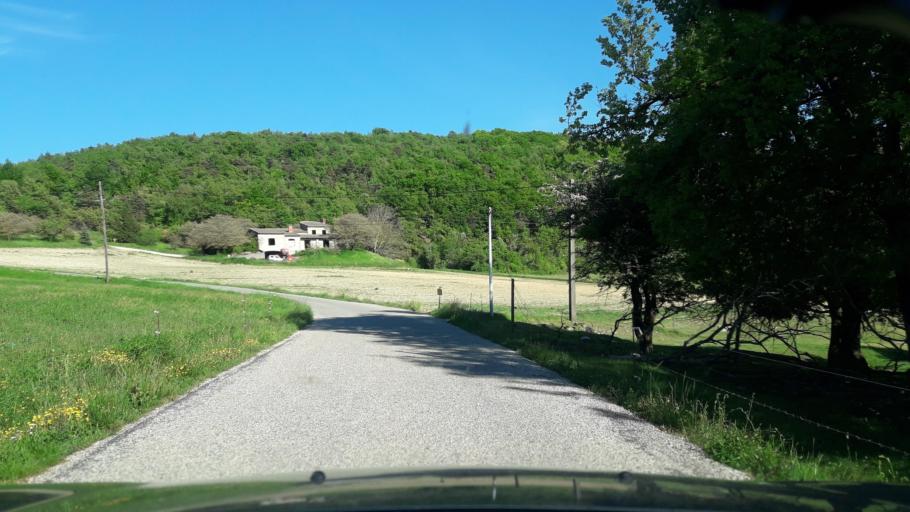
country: FR
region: Rhone-Alpes
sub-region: Departement de la Drome
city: Grane
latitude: 44.7054
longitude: 4.8847
